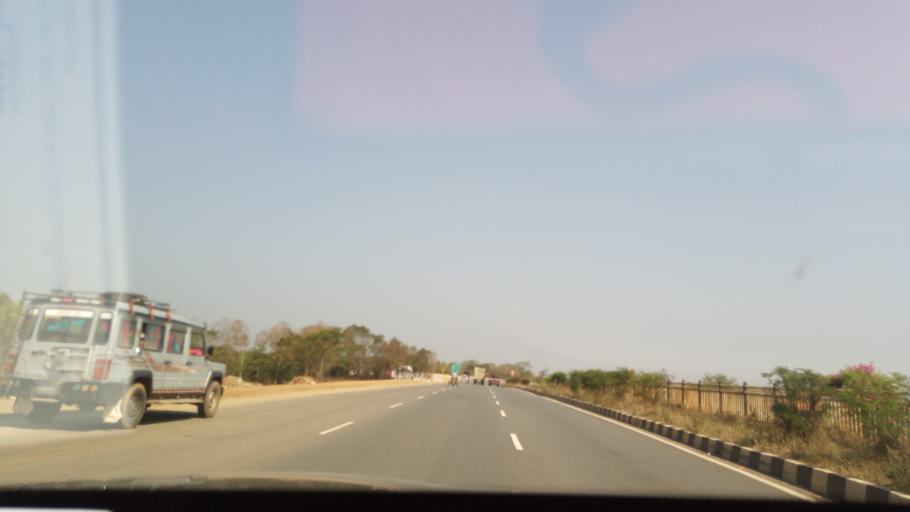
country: IN
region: Karnataka
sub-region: Dharwad
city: Kundgol
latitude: 15.2251
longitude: 75.1403
